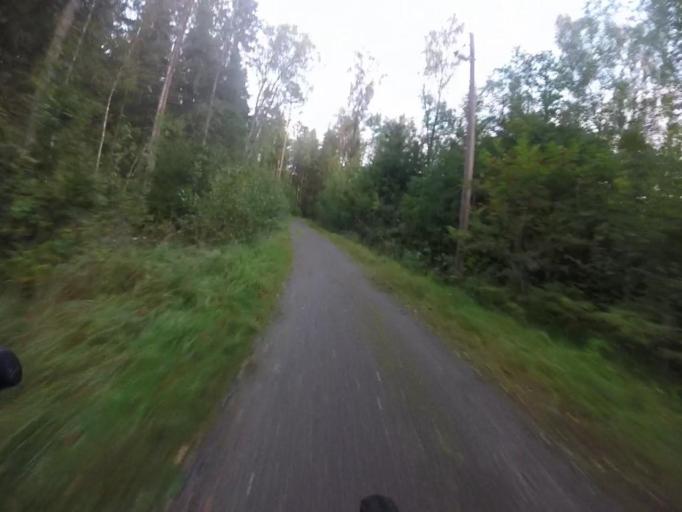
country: SE
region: Vaestra Goetaland
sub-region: Trollhattan
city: Trollhattan
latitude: 58.2998
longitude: 12.2580
